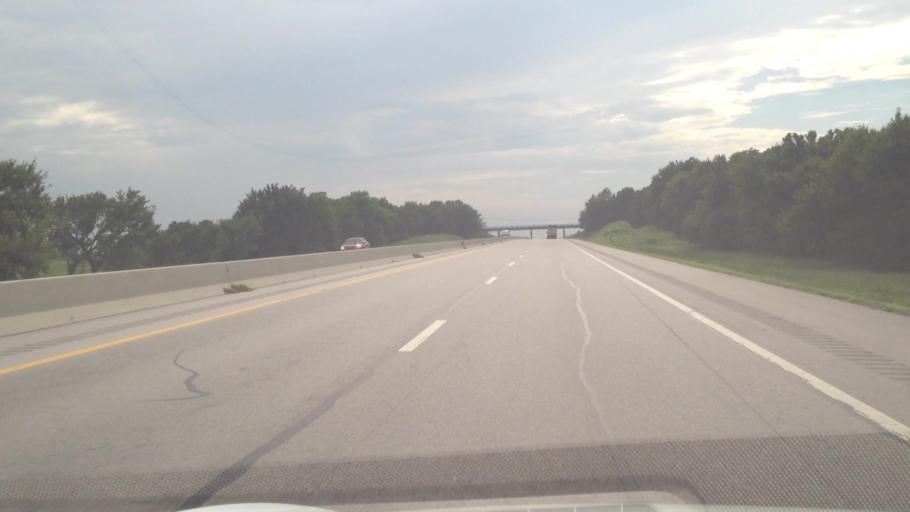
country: US
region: Kansas
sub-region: Cherokee County
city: Baxter Springs
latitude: 36.9355
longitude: -94.7082
